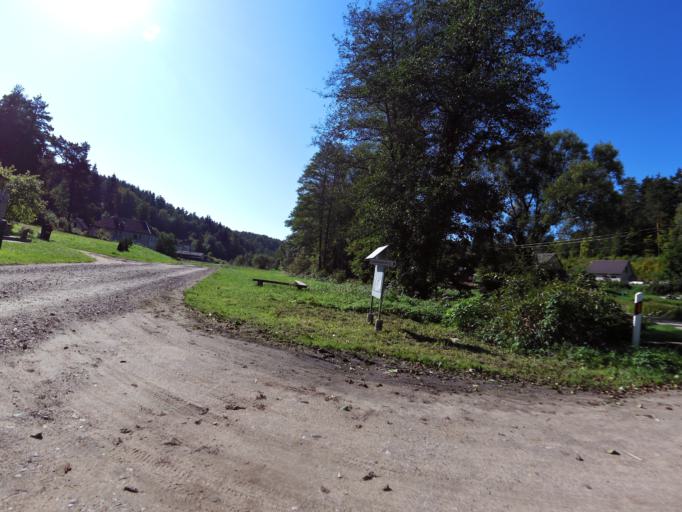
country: LT
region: Vilnius County
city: Pilaite
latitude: 54.6867
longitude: 25.1857
